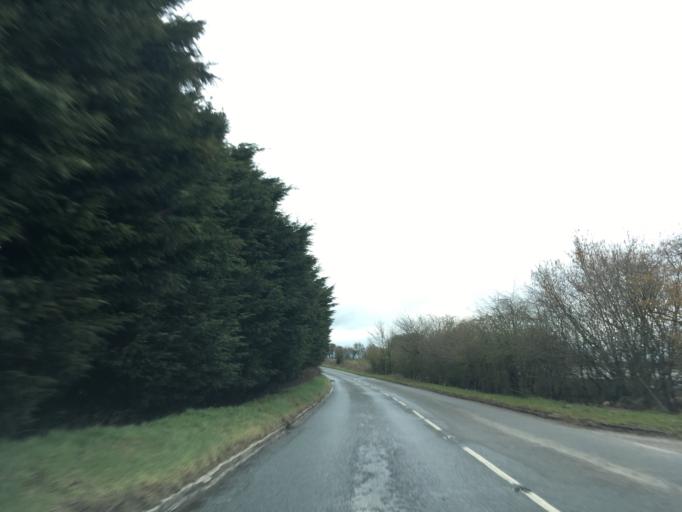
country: GB
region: England
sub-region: West Berkshire
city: Lambourn
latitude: 51.4901
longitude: -1.5723
